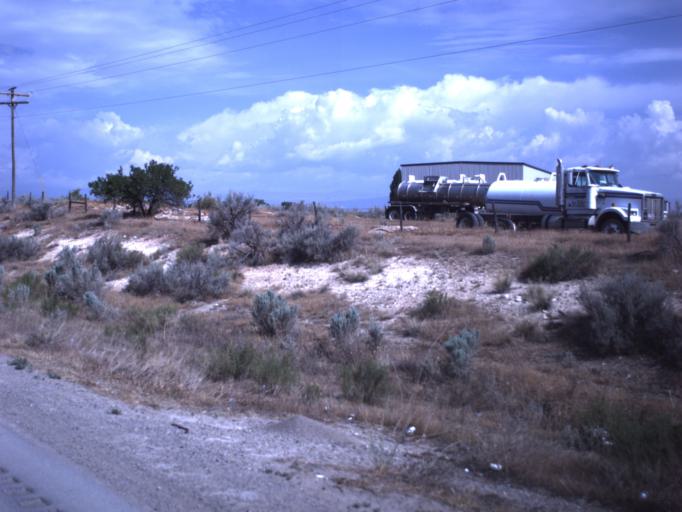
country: US
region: Utah
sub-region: Uintah County
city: Naples
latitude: 40.4026
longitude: -109.4720
